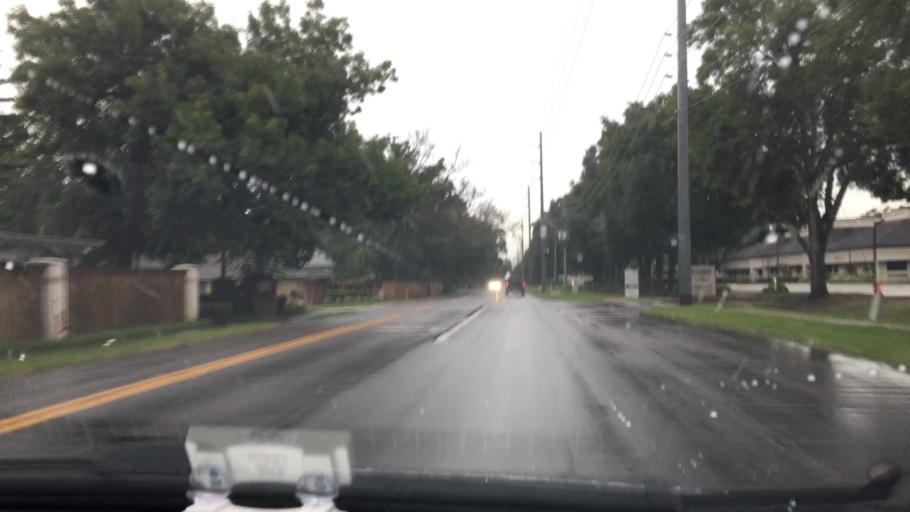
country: US
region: Florida
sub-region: Seminole County
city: Altamonte Springs
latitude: 28.6770
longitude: -81.3903
